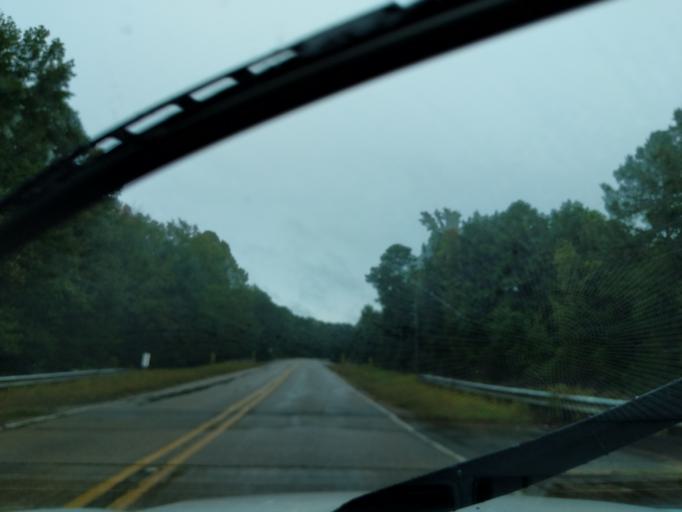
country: US
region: Louisiana
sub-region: Bienville Parish
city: Arcadia
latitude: 32.5534
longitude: -93.0533
